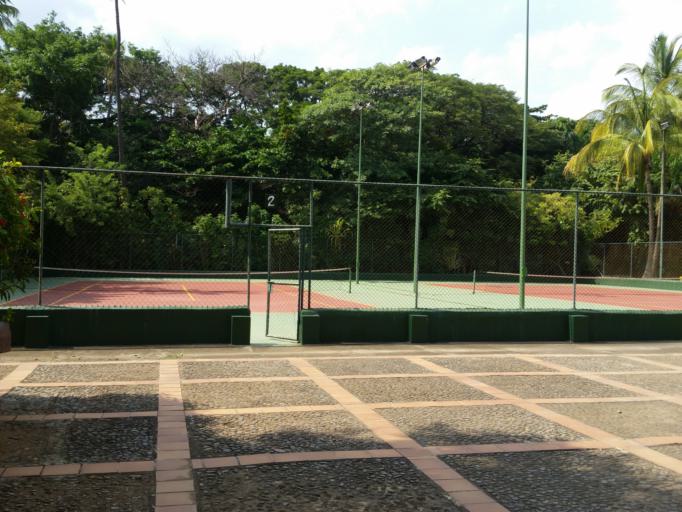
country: NI
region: Managua
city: Masachapa
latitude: 11.8099
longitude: -86.5224
